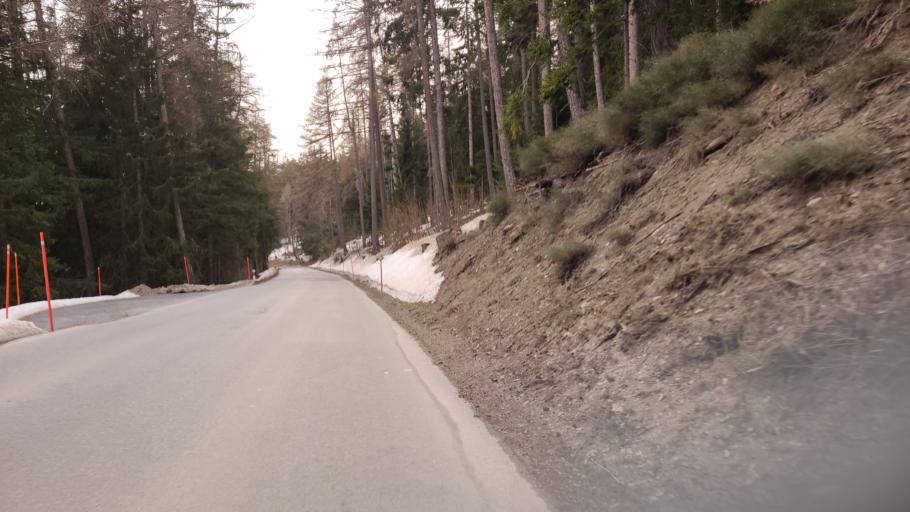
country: CH
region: Valais
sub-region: Sierre District
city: Montana
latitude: 46.3008
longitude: 7.4815
